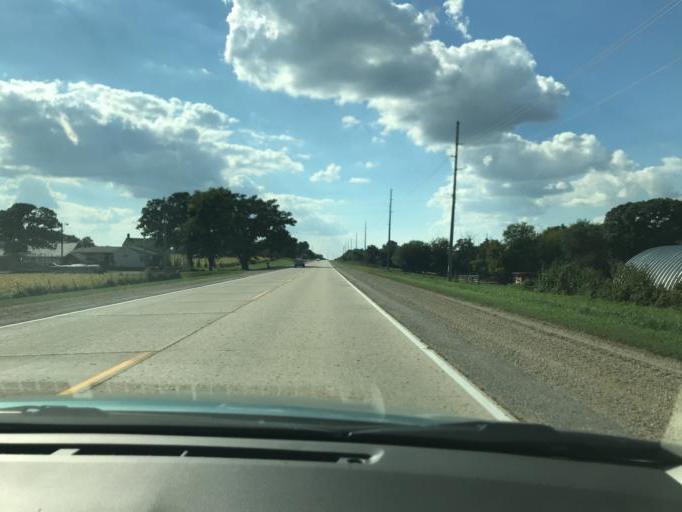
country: US
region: Wisconsin
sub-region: Rock County
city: Orfordville
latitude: 42.5573
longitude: -89.2927
